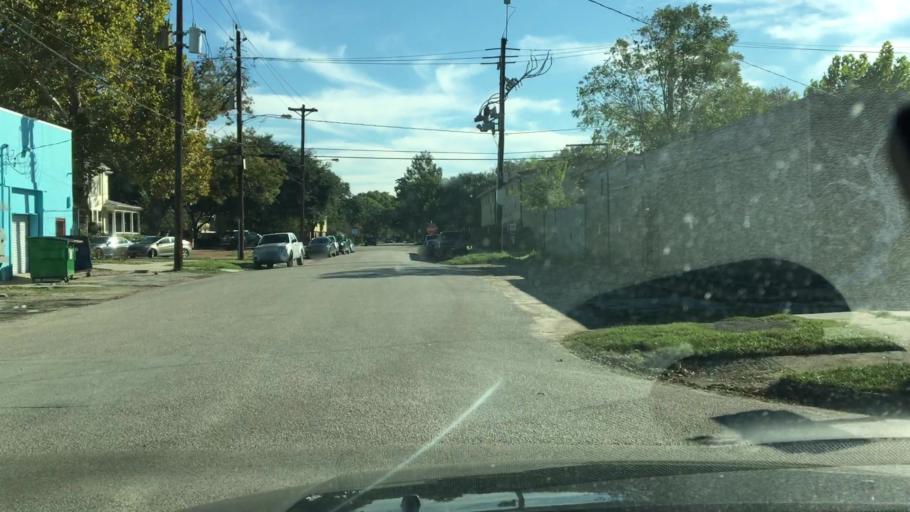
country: US
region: Texas
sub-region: Harris County
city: Houston
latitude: 29.7980
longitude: -95.3991
